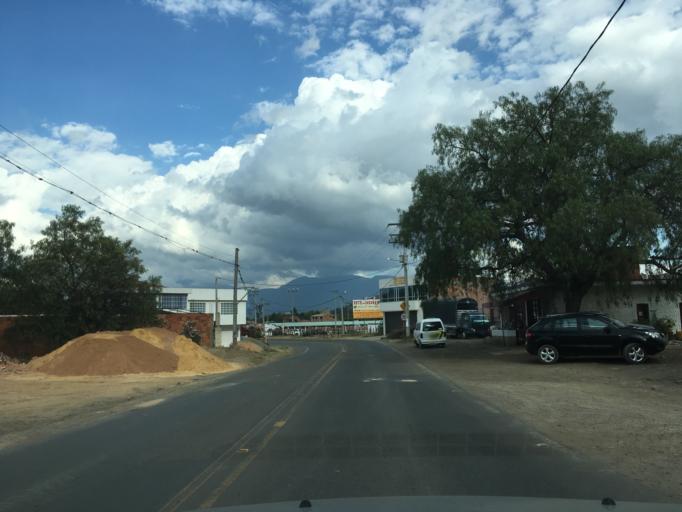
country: CO
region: Boyaca
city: Sutamarchan
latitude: 5.6169
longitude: -73.6223
